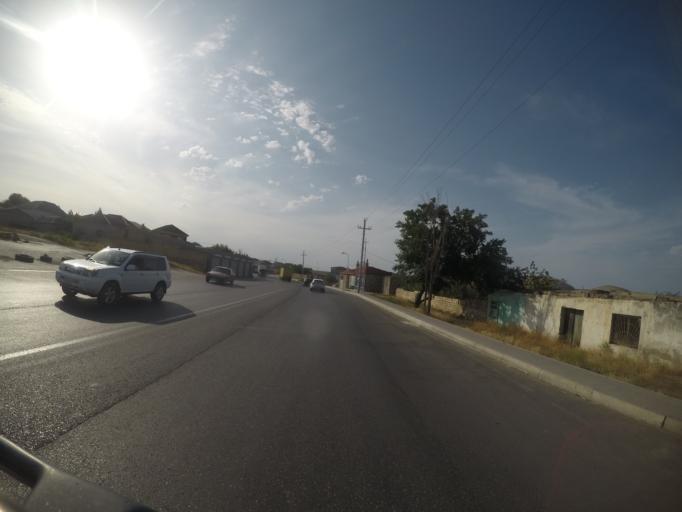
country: AZ
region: Baki
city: Binagadi
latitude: 40.4731
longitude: 49.8353
